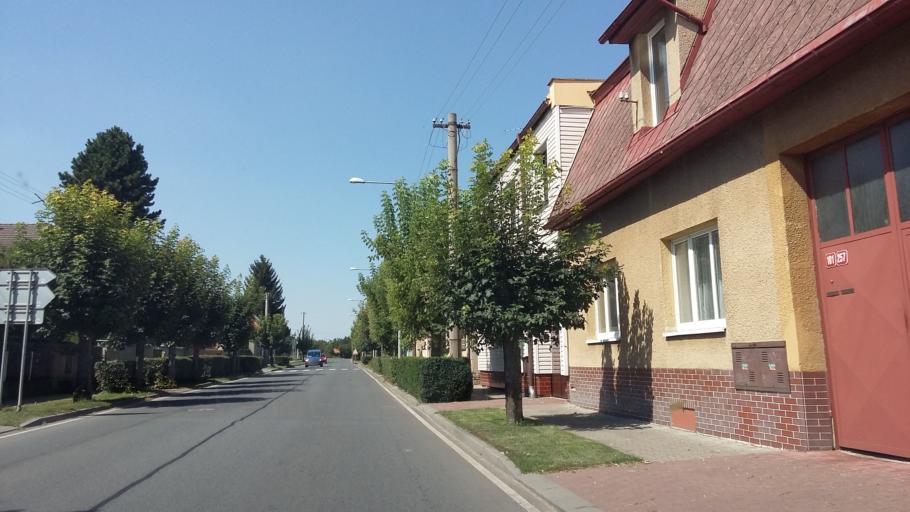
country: CZ
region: Central Bohemia
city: Brandys nad Labem-Stara Boleslav
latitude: 50.1649
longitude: 14.6782
